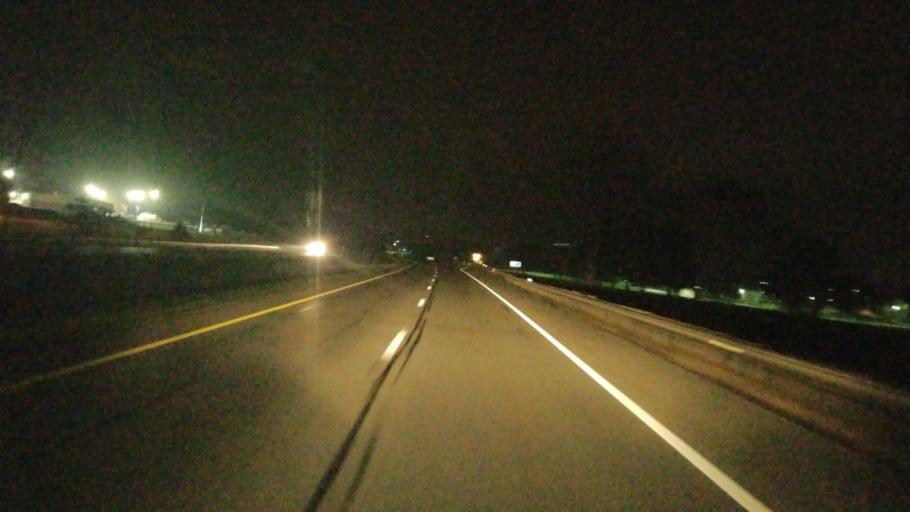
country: US
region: Ohio
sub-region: Stark County
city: Louisville
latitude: 40.8402
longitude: -81.3122
